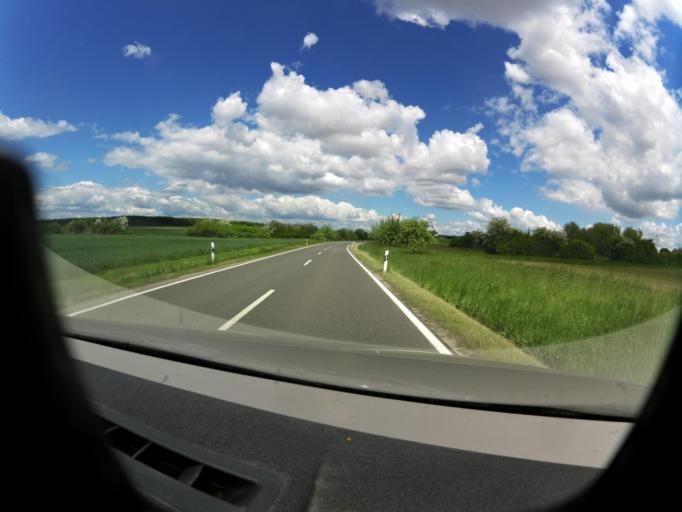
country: DE
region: Bavaria
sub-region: Regierungsbezirk Unterfranken
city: Prosselsheim
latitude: 49.8896
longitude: 10.1208
